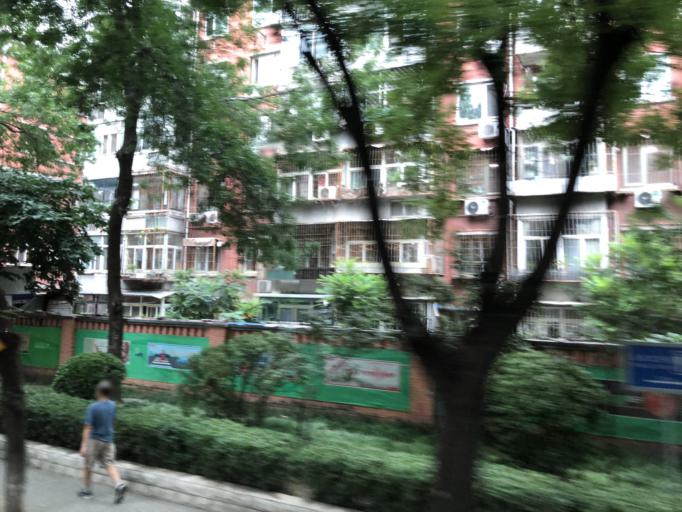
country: CN
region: Beijing
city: Jinrongjie
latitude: 39.9507
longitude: 116.3242
